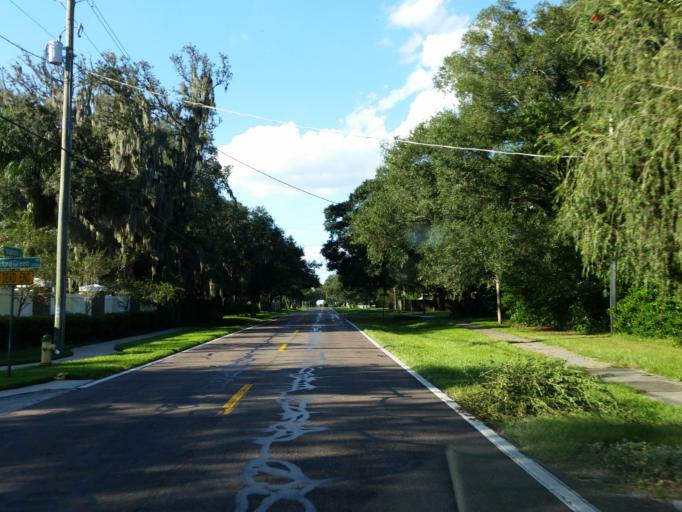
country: US
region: Florida
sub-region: Hillsborough County
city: Valrico
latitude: 27.9205
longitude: -82.2528
